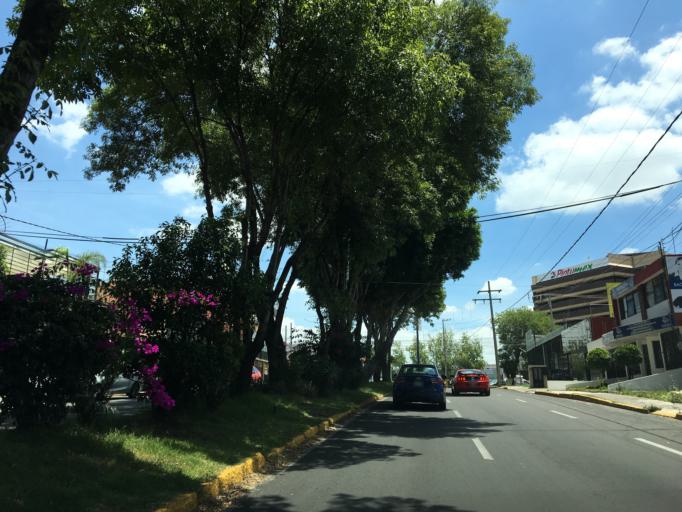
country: MX
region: Puebla
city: Puebla
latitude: 19.0543
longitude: -98.2198
